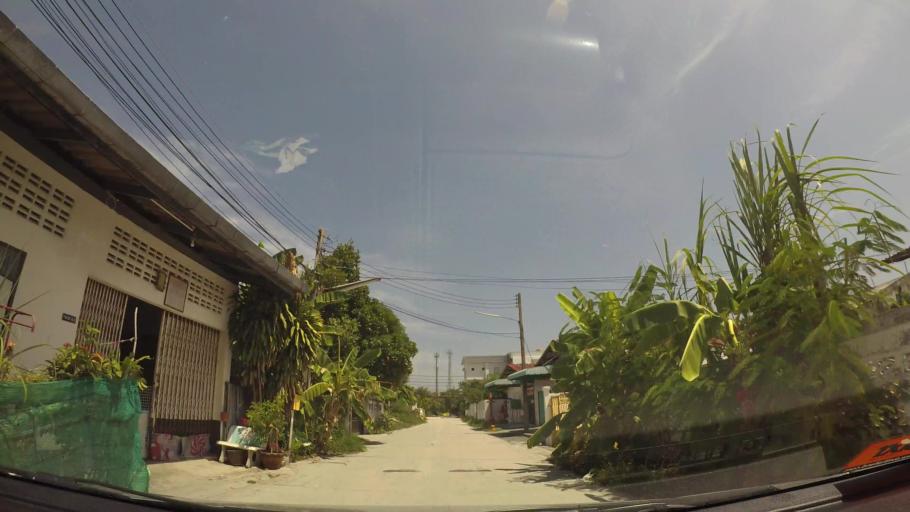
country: TH
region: Chon Buri
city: Chon Buri
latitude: 13.3201
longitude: 100.9559
